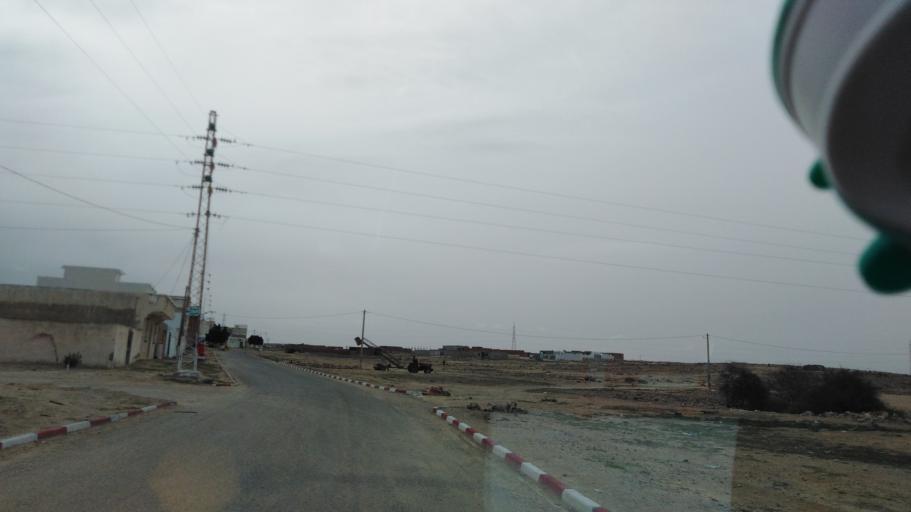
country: TN
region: Qabis
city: Gabes
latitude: 33.9522
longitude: 10.0030
